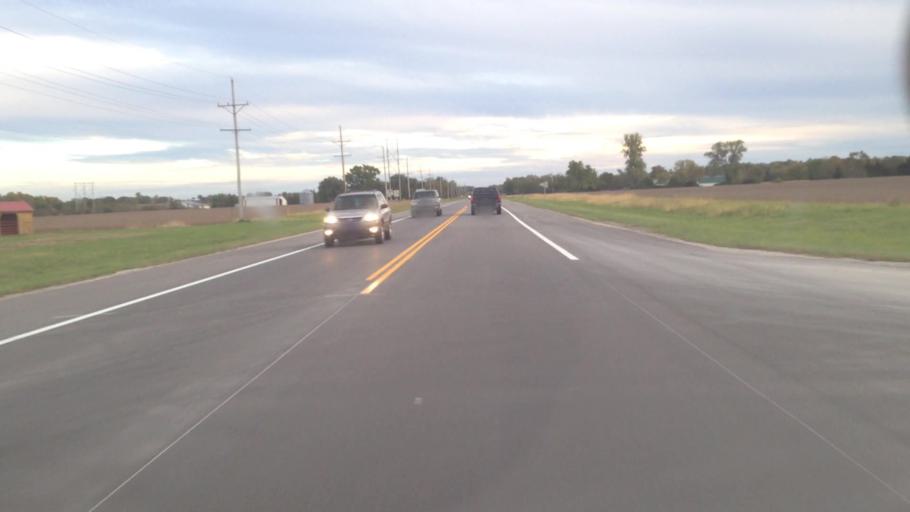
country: US
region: Kansas
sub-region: Franklin County
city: Ottawa
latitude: 38.5648
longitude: -95.2679
